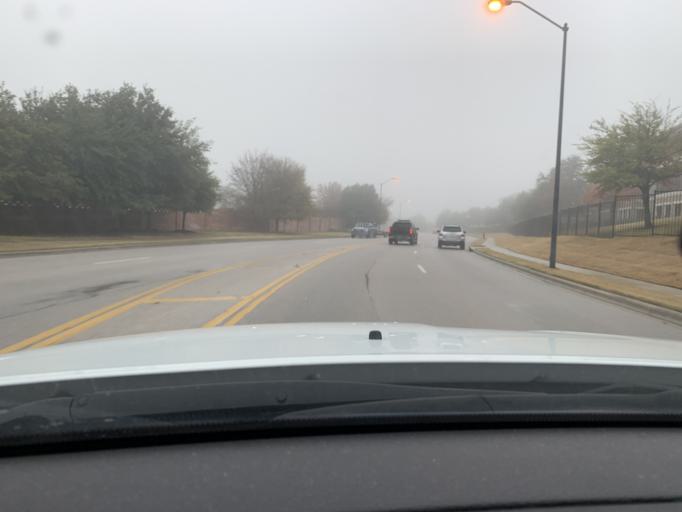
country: US
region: Texas
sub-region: Williamson County
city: Round Rock
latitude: 30.5678
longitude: -97.6835
